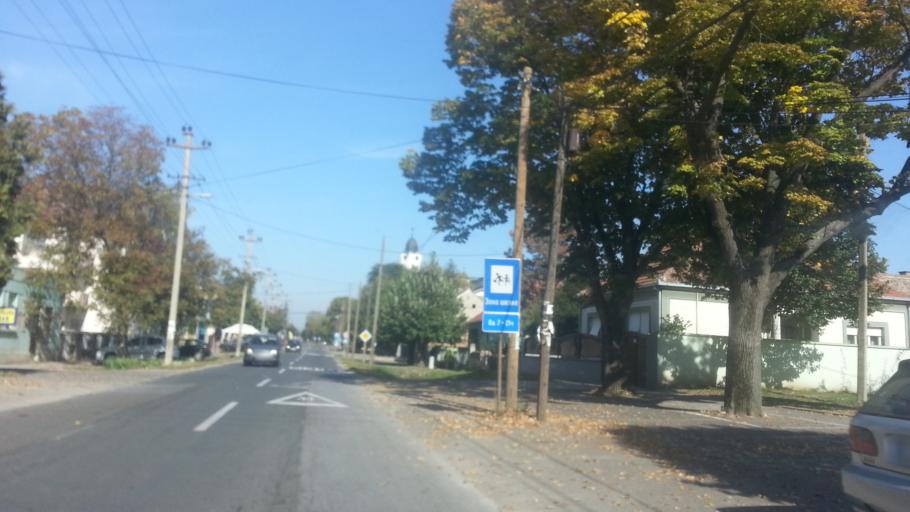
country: RS
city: Belegis
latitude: 45.0180
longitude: 20.3315
